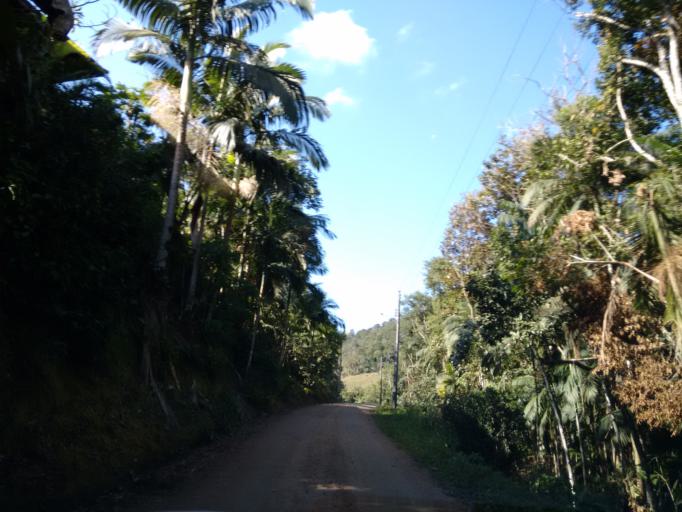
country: BR
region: Santa Catarina
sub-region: Pomerode
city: Pomerode
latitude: -26.7436
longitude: -49.1545
